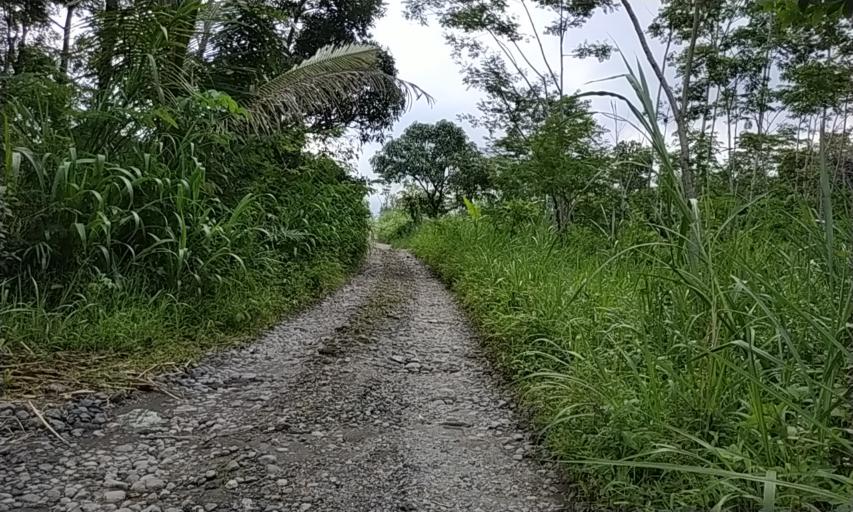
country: ID
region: Central Java
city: Jogonalan
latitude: -7.6307
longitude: 110.4859
